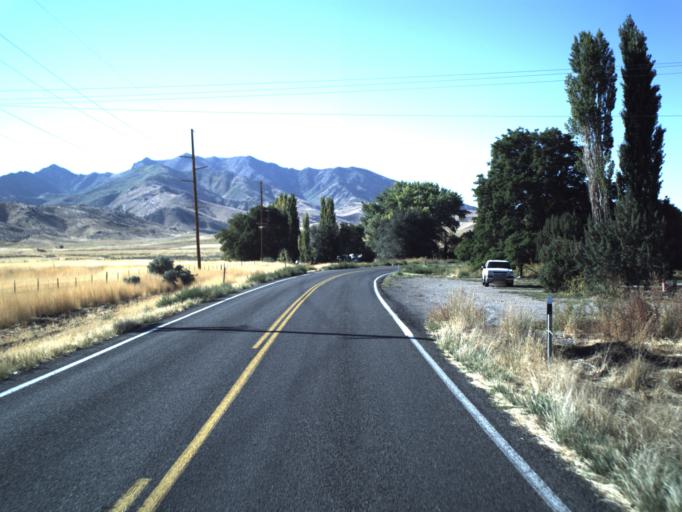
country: US
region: Utah
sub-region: Millard County
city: Delta
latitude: 39.4737
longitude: -112.2688
